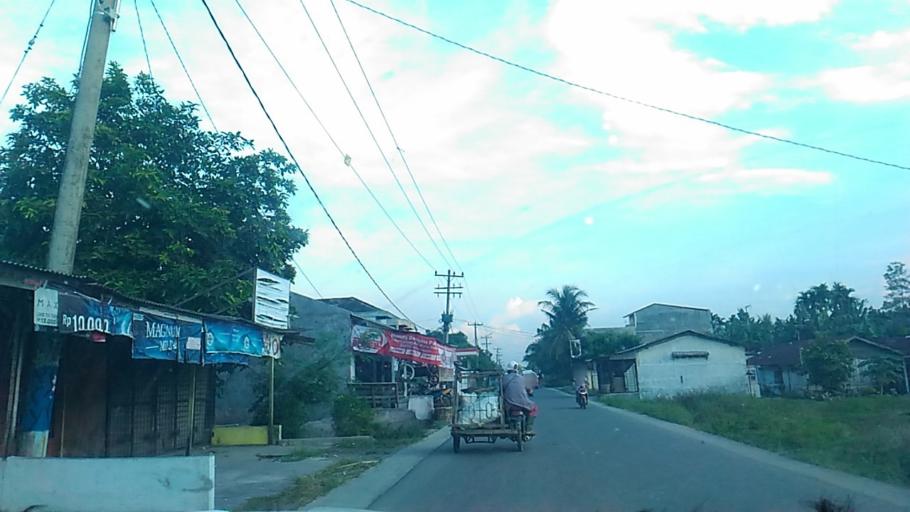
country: ID
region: North Sumatra
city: Labuhan Deli
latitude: 3.6826
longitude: 98.5965
